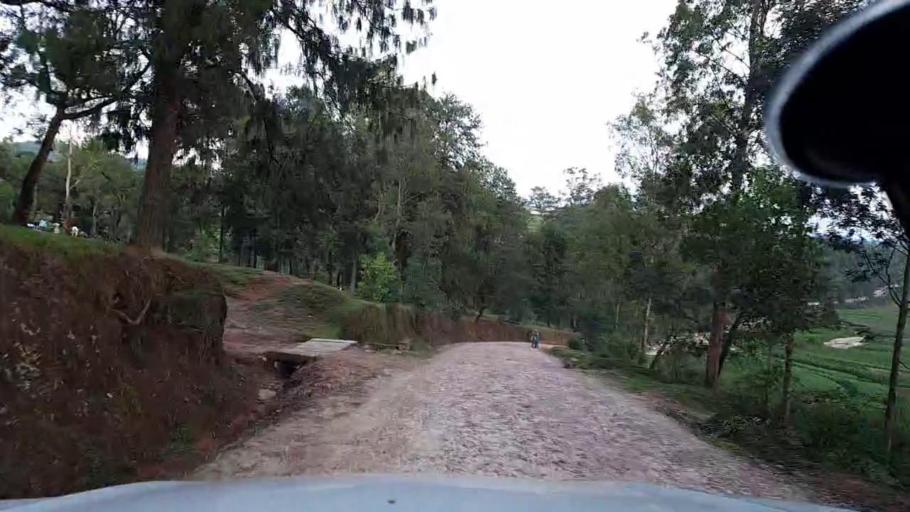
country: RW
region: Southern Province
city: Nyanza
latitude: -2.2156
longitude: 29.6413
